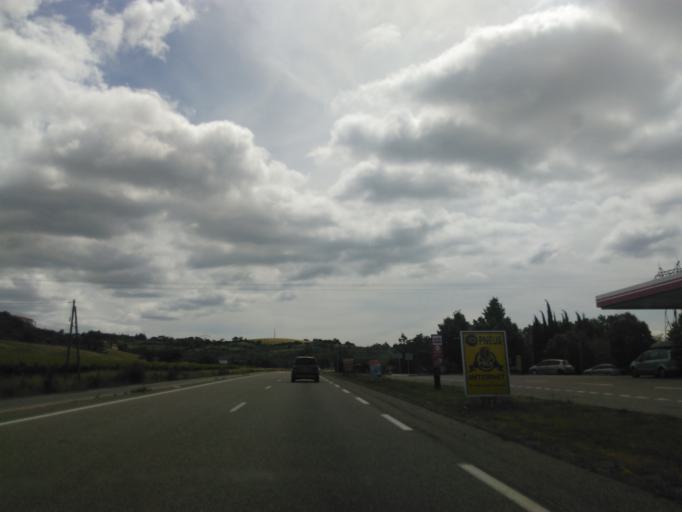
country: FR
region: Rhone-Alpes
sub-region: Departement de l'Ardeche
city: Villeneuve-de-Berg
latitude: 44.5867
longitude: 4.5348
